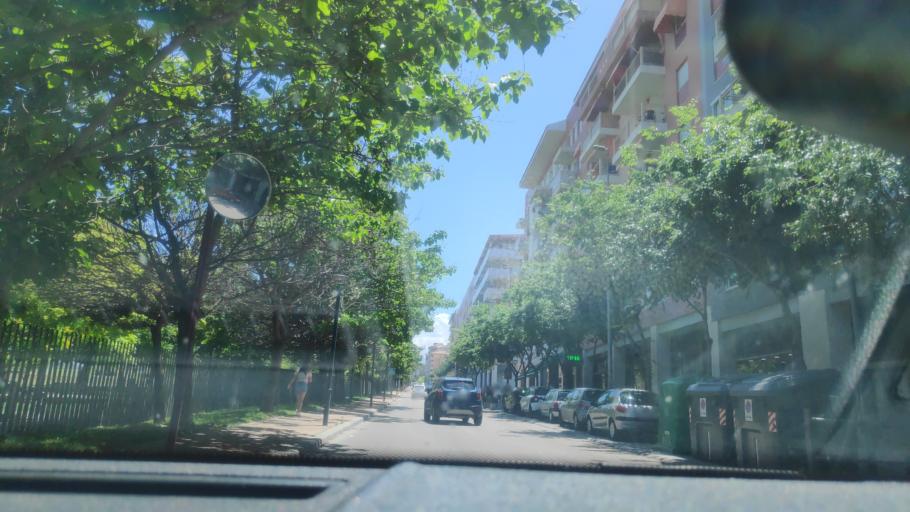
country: ES
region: Andalusia
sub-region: Provincia de Jaen
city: Jaen
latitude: 37.7873
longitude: -3.7916
